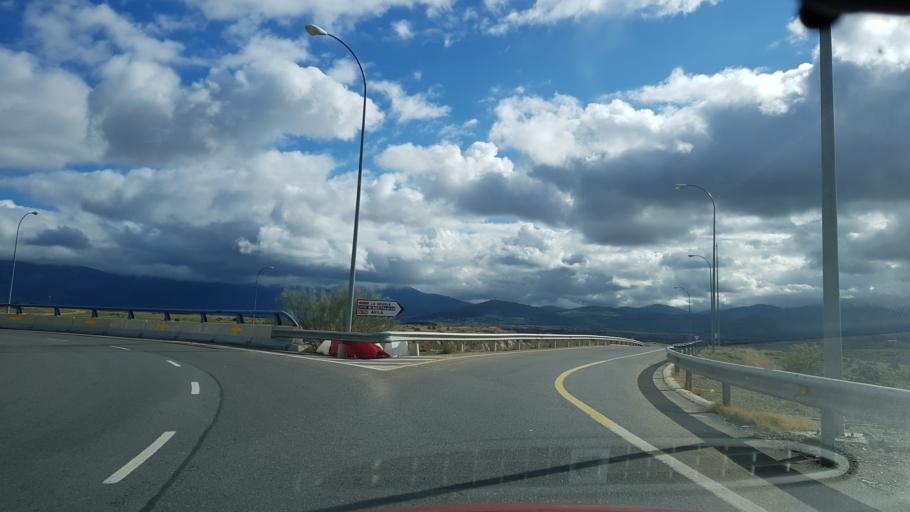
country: ES
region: Castille and Leon
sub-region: Provincia de Segovia
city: San Cristobal de Segovia
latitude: 40.9524
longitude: -4.0913
